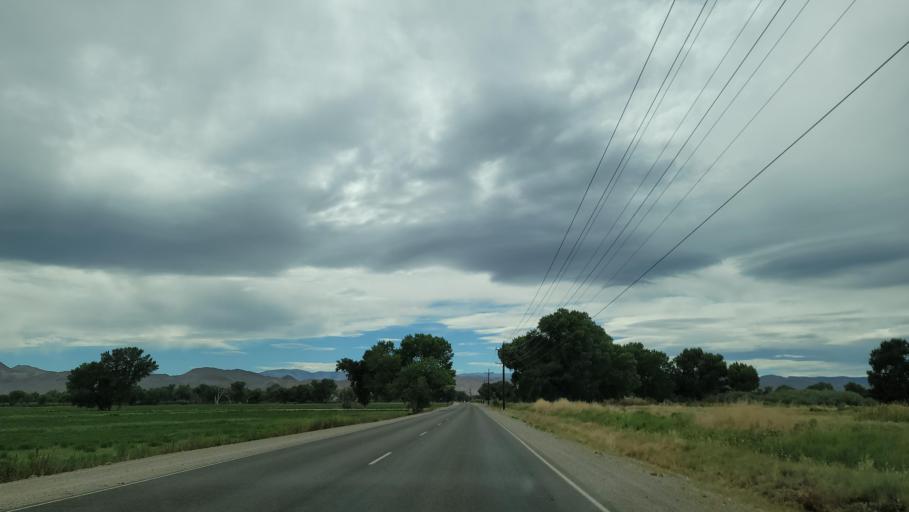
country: US
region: Nevada
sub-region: Lyon County
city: Yerington
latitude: 39.0482
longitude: -119.1551
